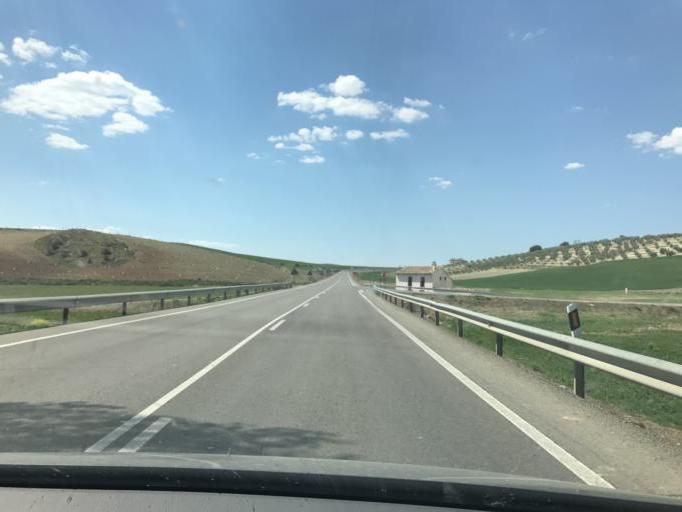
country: ES
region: Andalusia
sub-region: Provincia de Jaen
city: Frailes
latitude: 37.4391
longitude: -3.8446
